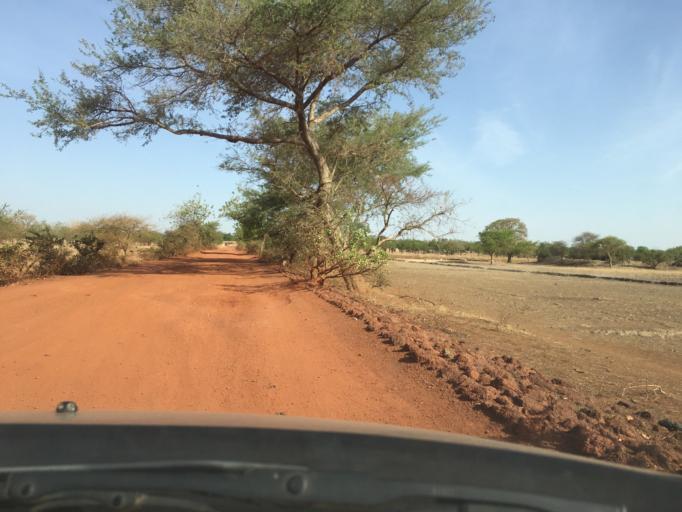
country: BF
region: Plateau-Central
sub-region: Province du Kourweogo
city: Bousse
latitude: 12.5715
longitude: -1.9283
